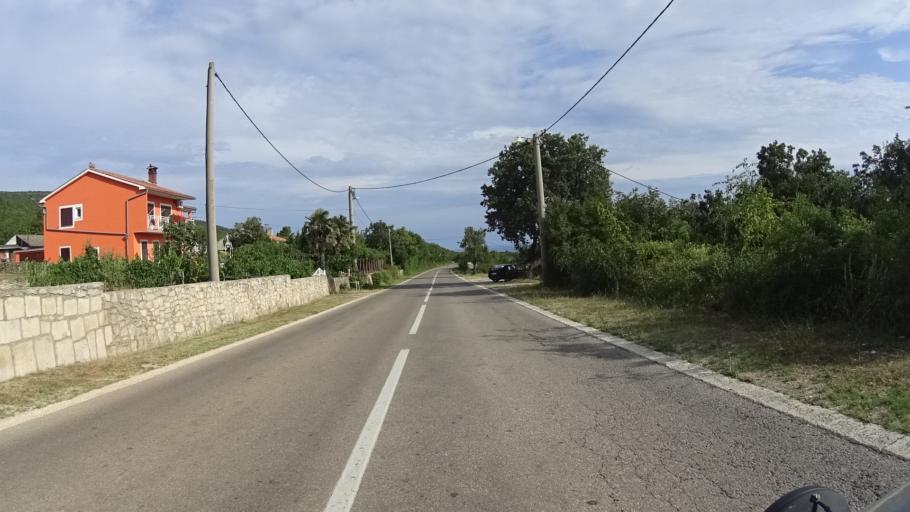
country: HR
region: Istarska
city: Rasa
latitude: 45.0033
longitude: 14.0999
